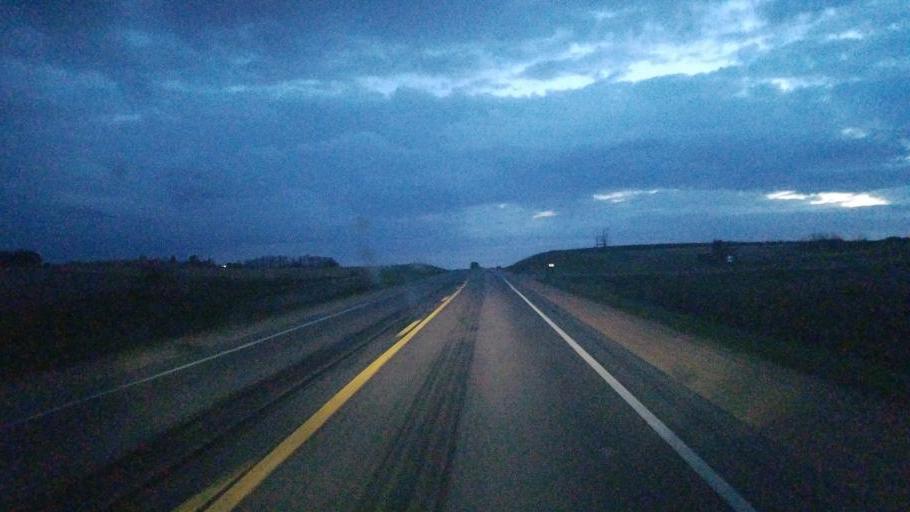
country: US
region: Wisconsin
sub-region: Vernon County
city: Hillsboro
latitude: 43.6385
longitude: -90.3572
